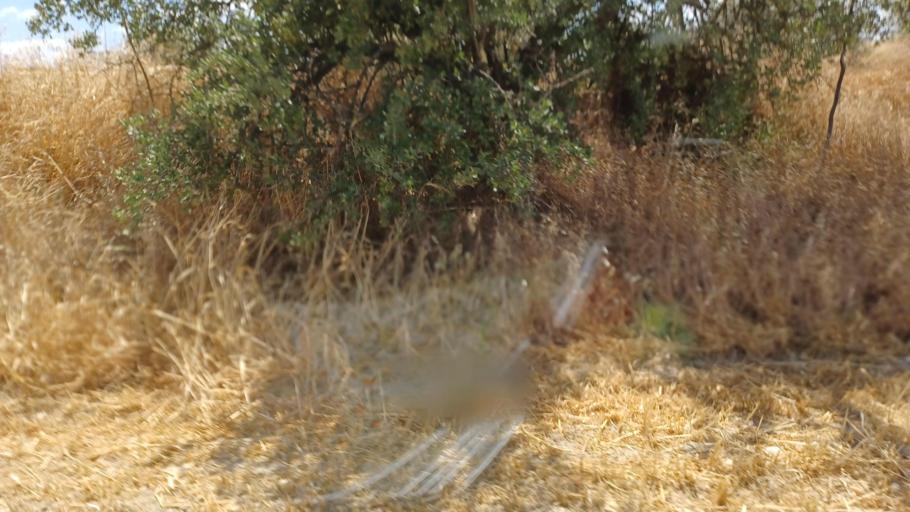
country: CY
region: Larnaka
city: Athienou
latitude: 35.0521
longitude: 33.5456
